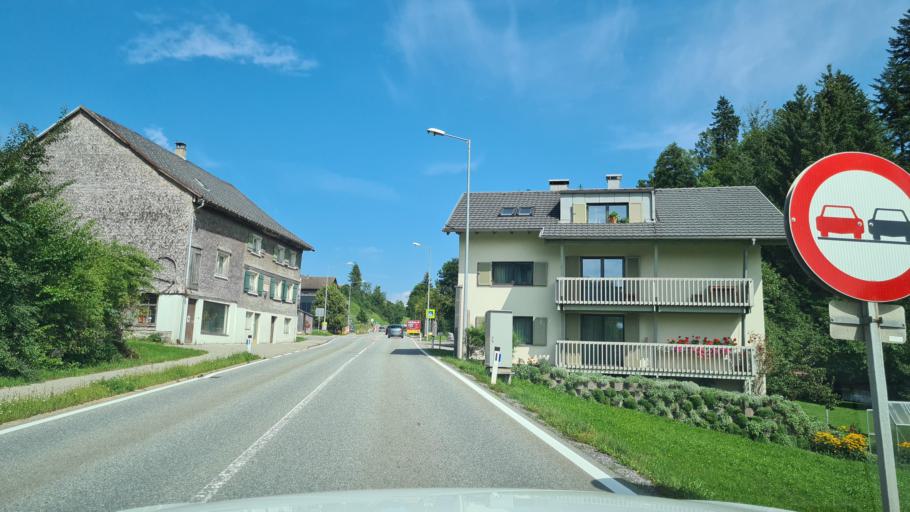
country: AT
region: Vorarlberg
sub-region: Politischer Bezirk Bregenz
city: Bildstein
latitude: 47.4514
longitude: 9.8197
